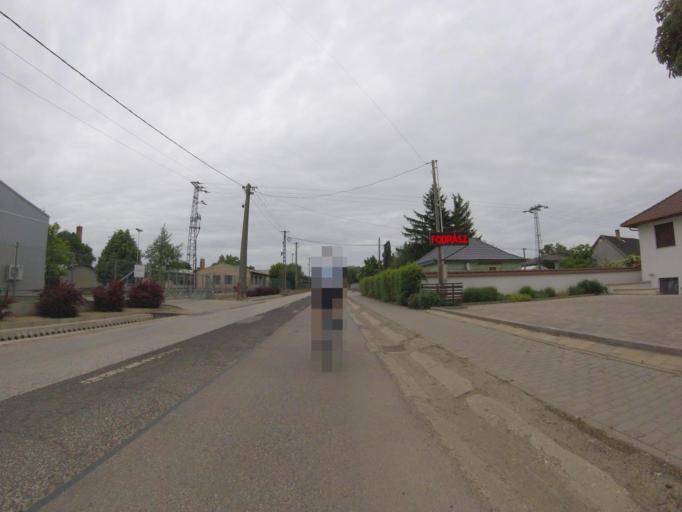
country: HU
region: Pest
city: Dabas
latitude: 47.1776
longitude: 19.3423
